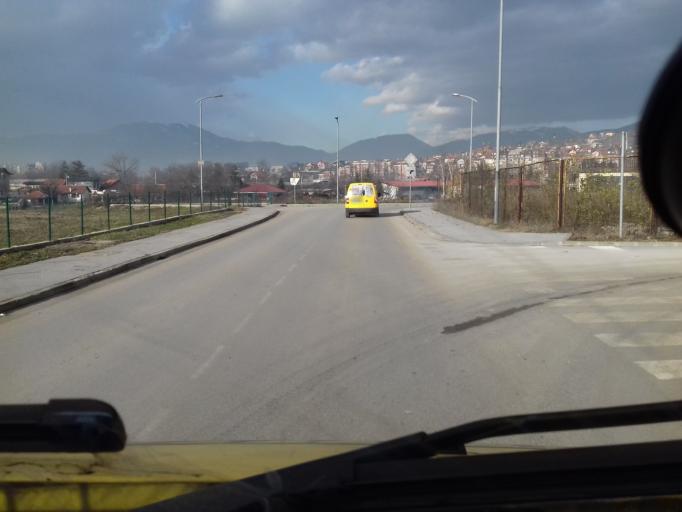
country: BA
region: Federation of Bosnia and Herzegovina
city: Zenica
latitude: 44.1895
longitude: 17.9296
